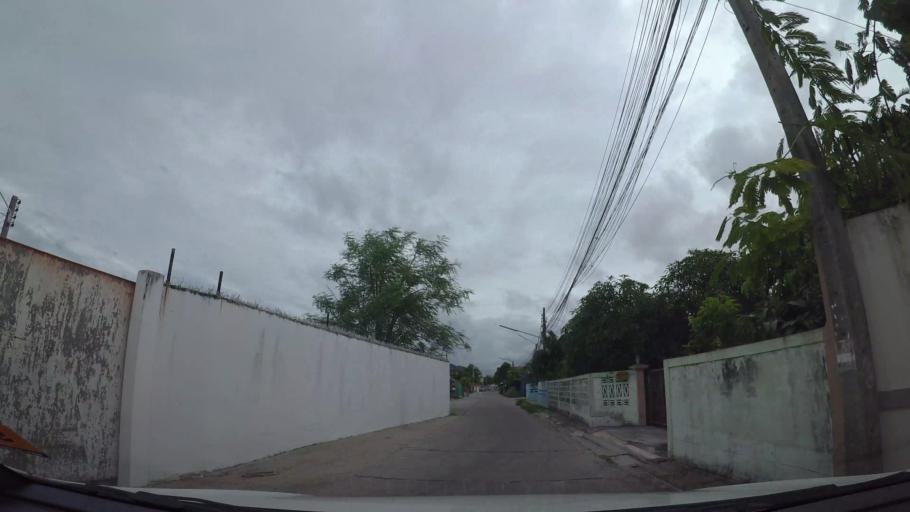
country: TH
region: Rayong
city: Rayong
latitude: 12.6638
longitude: 101.2697
